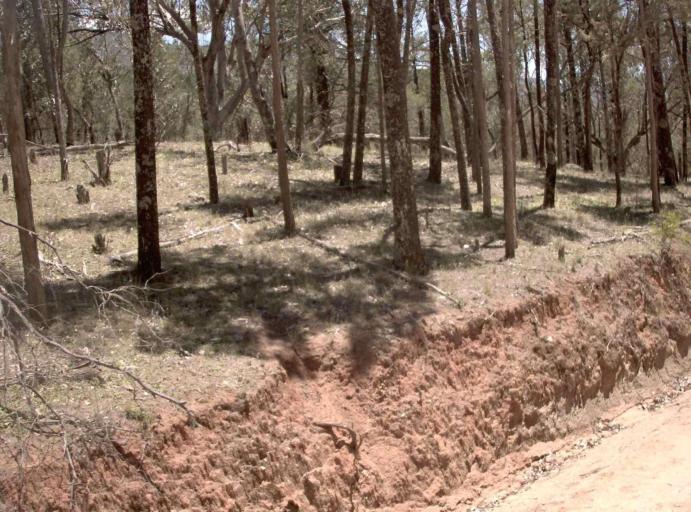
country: AU
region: New South Wales
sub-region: Snowy River
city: Jindabyne
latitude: -36.8907
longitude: 148.4214
